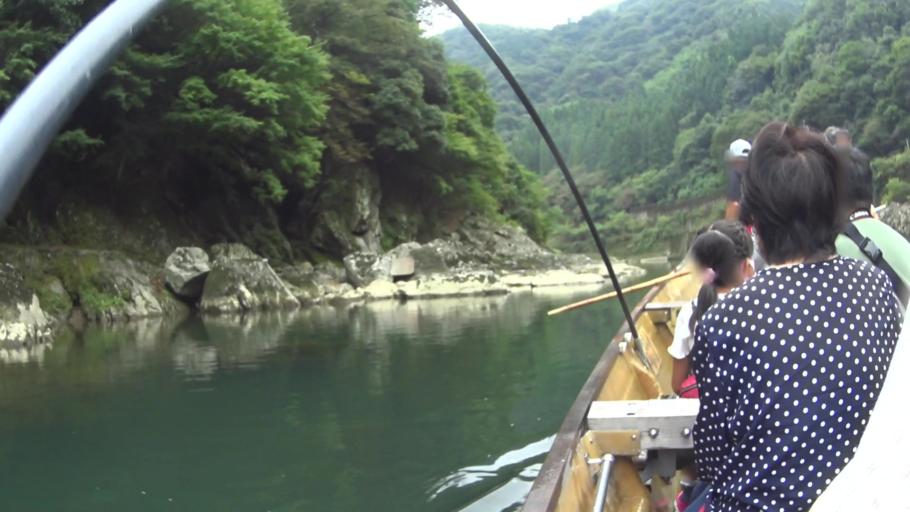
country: JP
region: Kyoto
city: Kameoka
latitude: 35.0195
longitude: 135.6227
